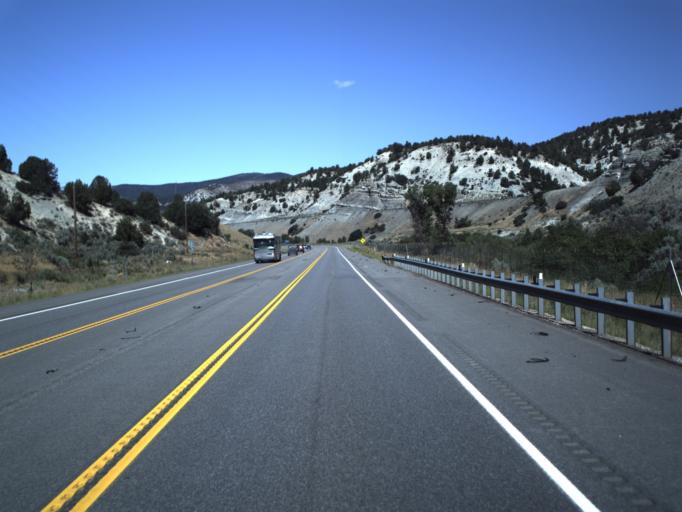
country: US
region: Utah
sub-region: Sanpete County
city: Fairview
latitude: 39.9429
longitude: -111.2019
